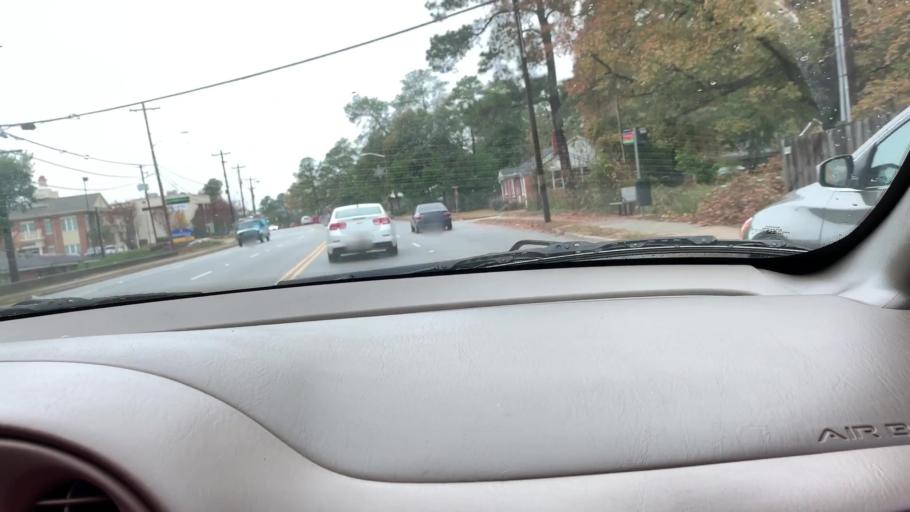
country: US
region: South Carolina
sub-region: Richland County
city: Forest Acres
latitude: 34.0210
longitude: -80.9792
